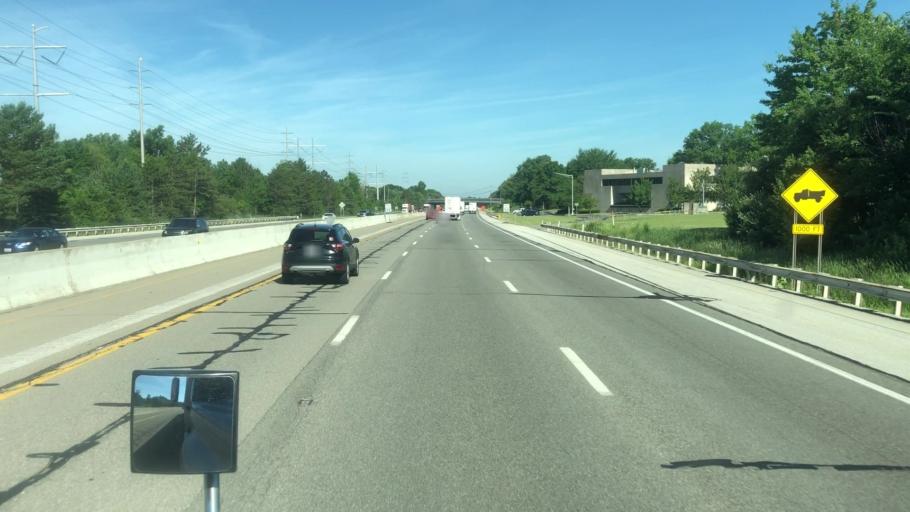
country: US
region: Ohio
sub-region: Cuyahoga County
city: Berea
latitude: 41.3477
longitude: -81.8591
